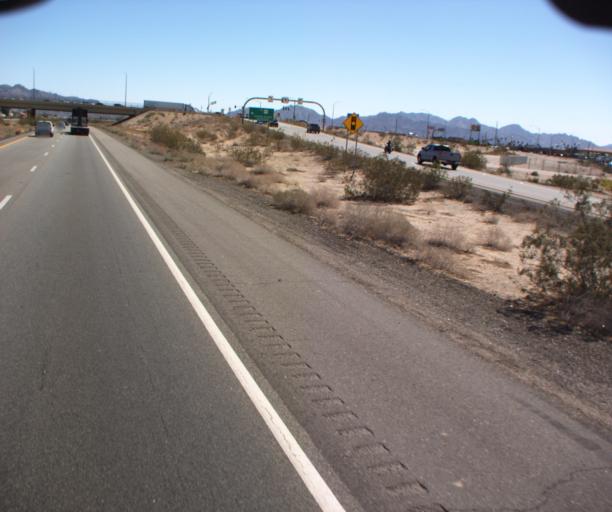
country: US
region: Arizona
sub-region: Yuma County
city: Fortuna Foothills
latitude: 32.6704
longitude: -114.4470
